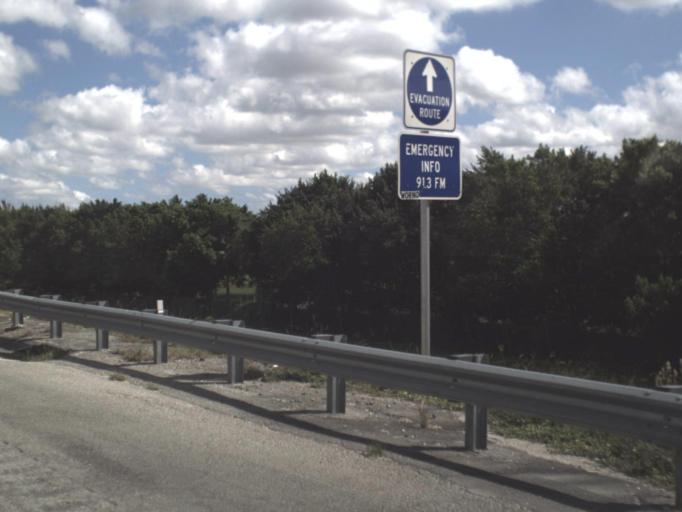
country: US
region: Florida
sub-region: Miami-Dade County
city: Country Club
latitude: 25.9631
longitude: -80.3337
